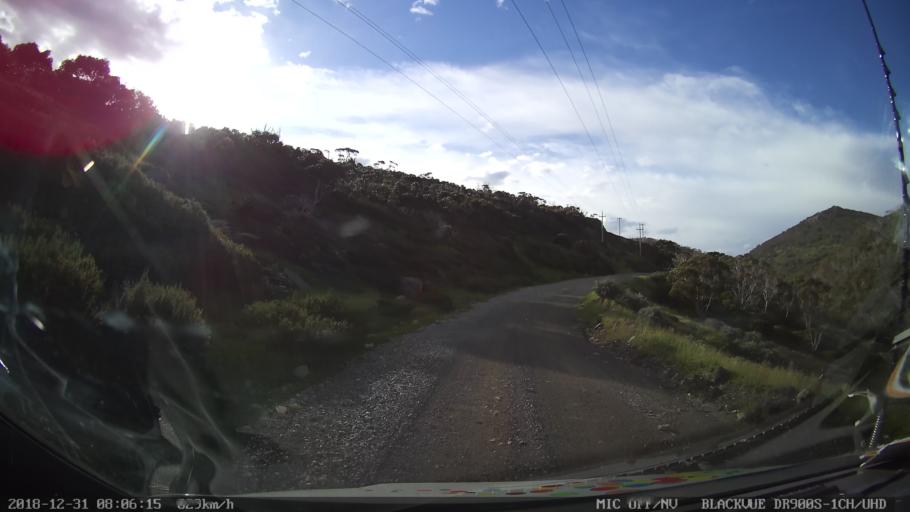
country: AU
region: New South Wales
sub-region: Snowy River
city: Jindabyne
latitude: -36.3739
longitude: 148.4079
